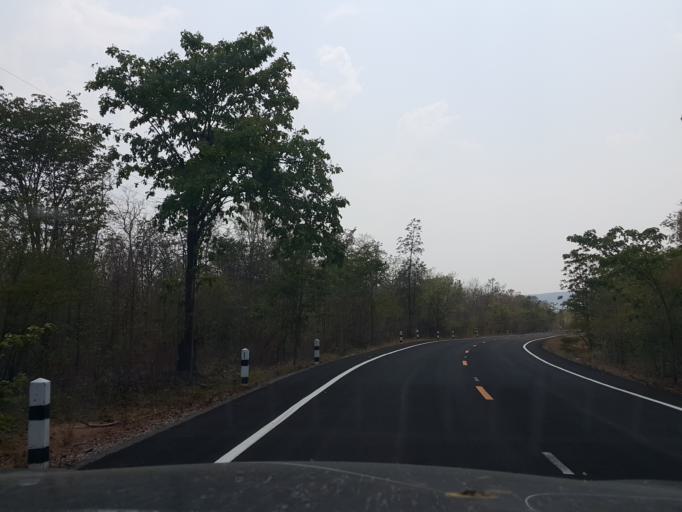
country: TH
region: Lampang
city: Mae Phrik
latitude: 17.4883
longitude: 99.1024
